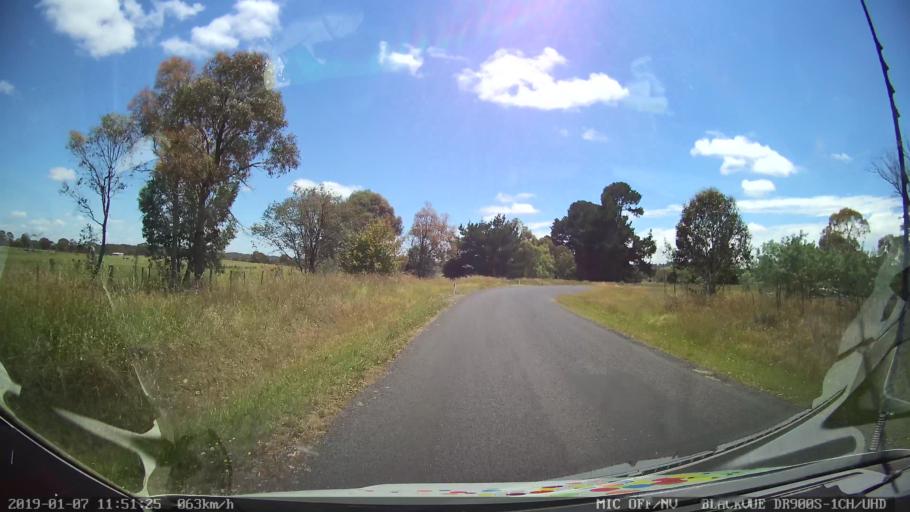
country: AU
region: New South Wales
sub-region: Guyra
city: Guyra
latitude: -30.3083
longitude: 151.6453
